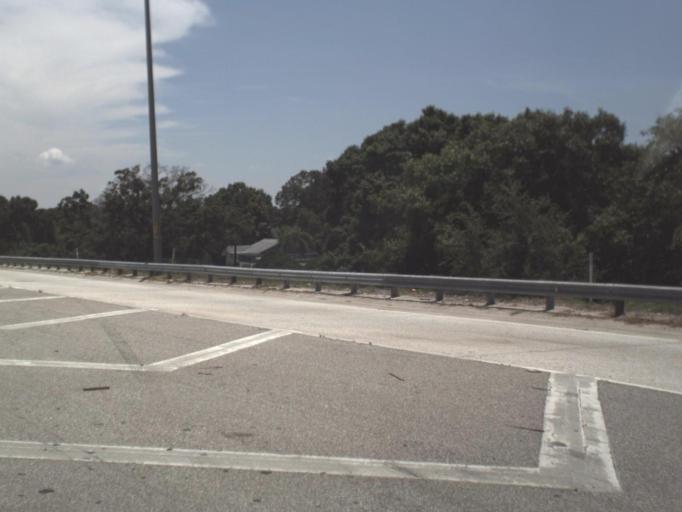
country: US
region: Florida
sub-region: Pinellas County
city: Saint Petersburg
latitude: 27.7808
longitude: -82.6609
